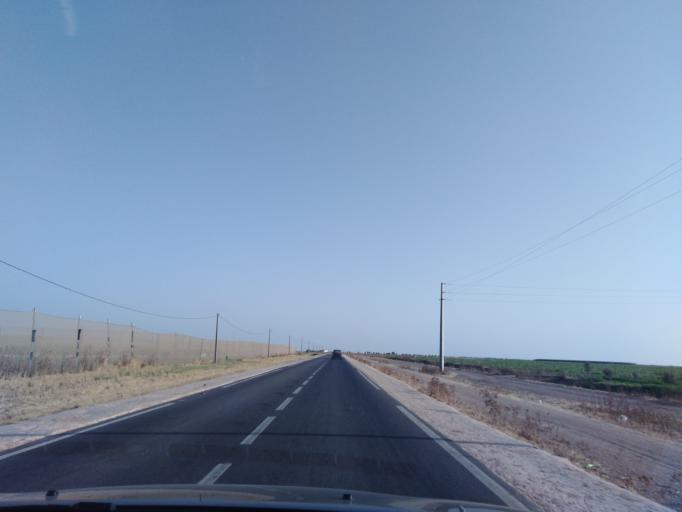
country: MA
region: Doukkala-Abda
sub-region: El-Jadida
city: Sidi Bennour
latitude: 32.5174
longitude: -8.7425
